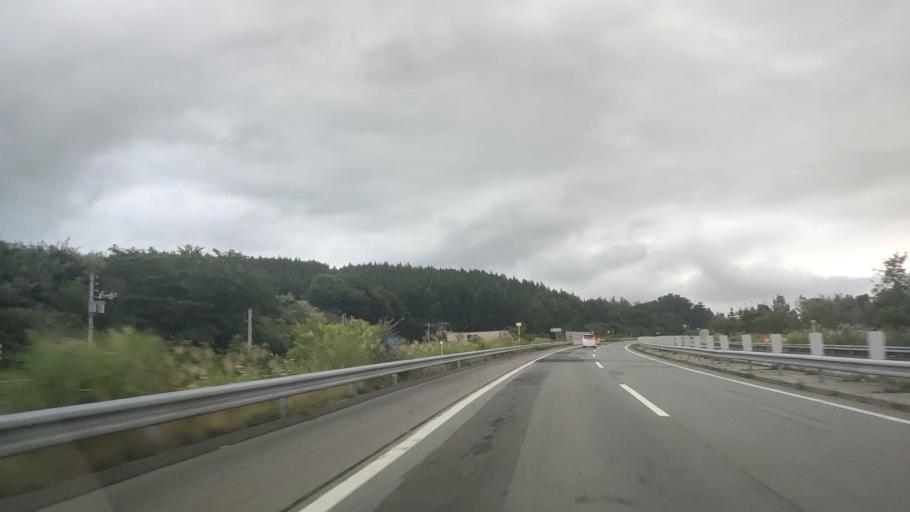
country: JP
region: Hokkaido
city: Nanae
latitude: 41.8997
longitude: 140.7047
